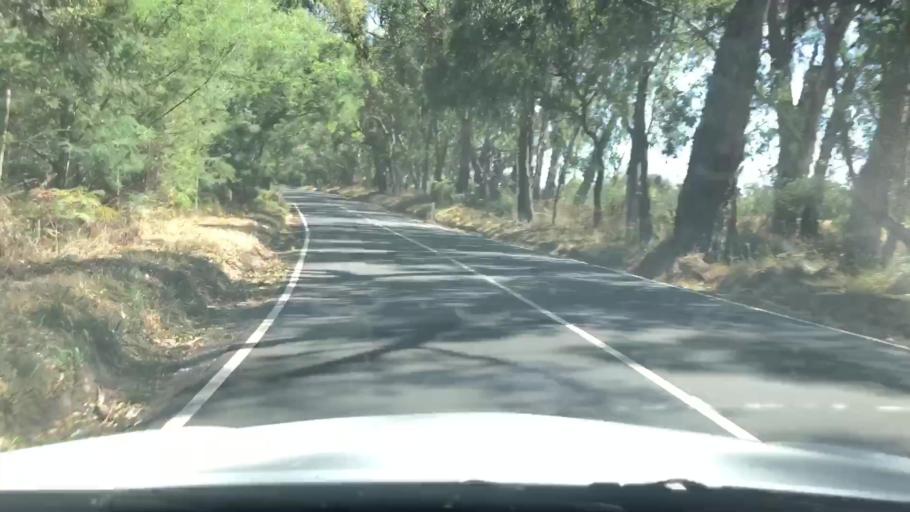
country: AU
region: Victoria
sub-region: Yarra Ranges
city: Woori Yallock
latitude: -37.8151
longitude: 145.5001
